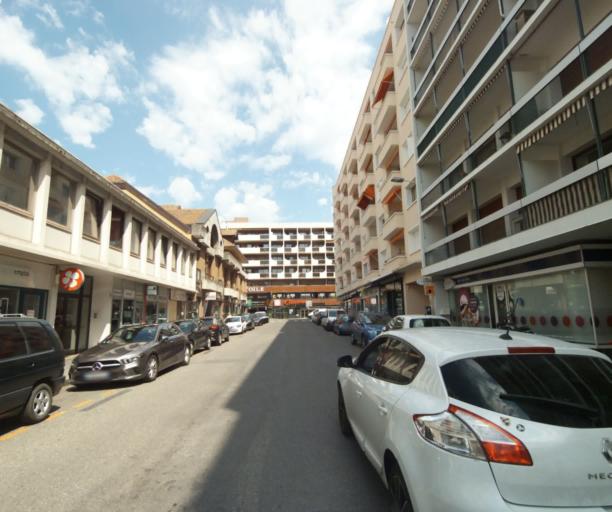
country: FR
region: Rhone-Alpes
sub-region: Departement de la Haute-Savoie
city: Thonon-les-Bains
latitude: 46.3693
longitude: 6.4778
